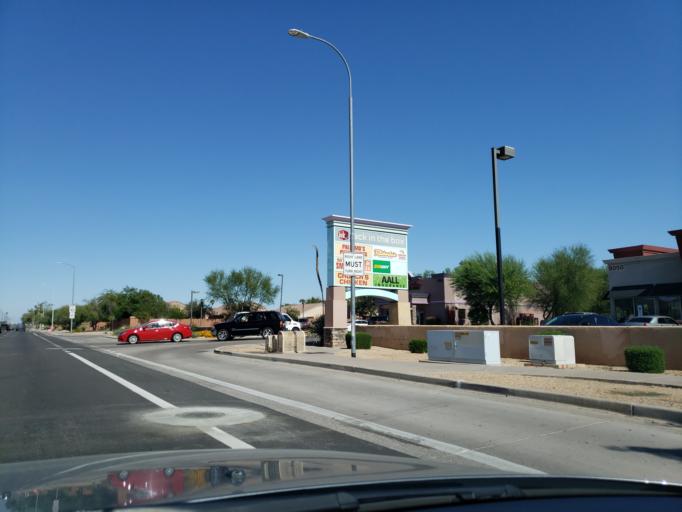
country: US
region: Arizona
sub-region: Maricopa County
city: Tolleson
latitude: 33.4811
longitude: -112.2551
